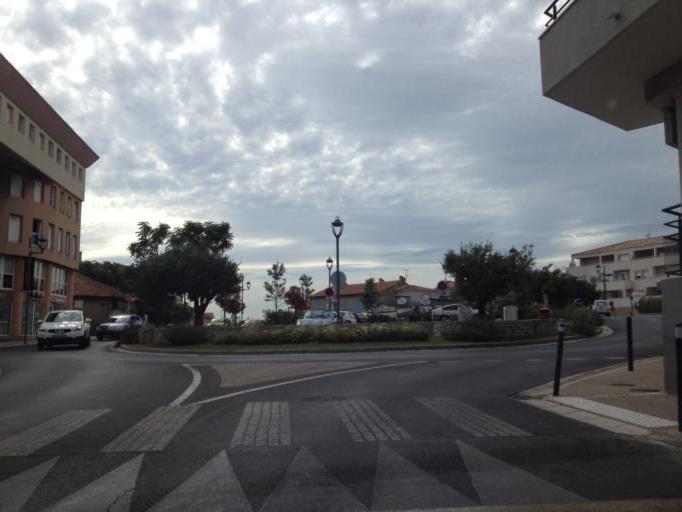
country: FR
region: Languedoc-Roussillon
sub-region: Departement du Gard
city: Les Angles
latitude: 43.9582
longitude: 4.7767
